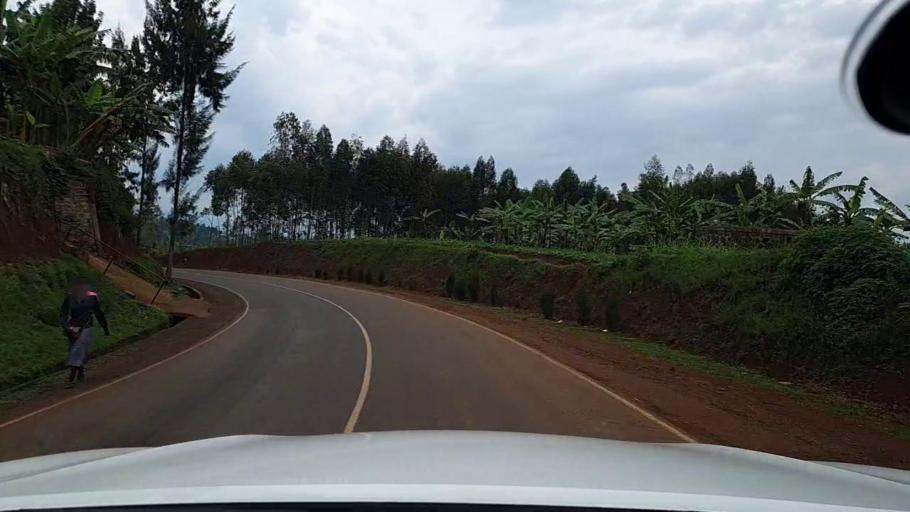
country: RW
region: Western Province
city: Cyangugu
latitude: -2.6446
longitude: 28.9539
